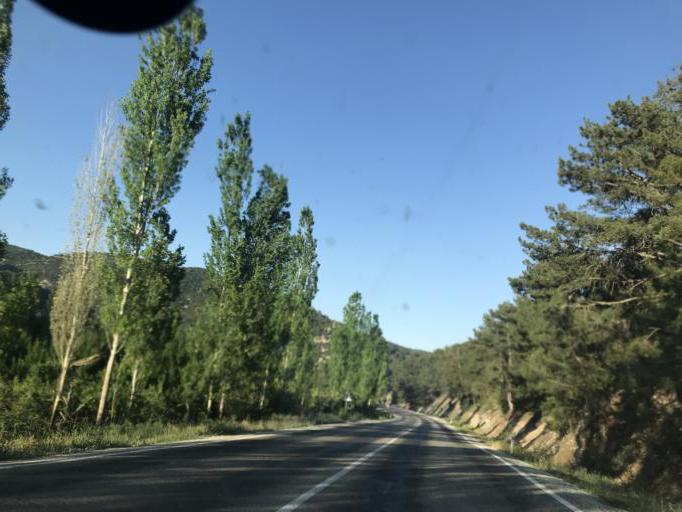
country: TR
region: Antalya
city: Korkuteli
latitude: 37.1286
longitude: 30.0756
